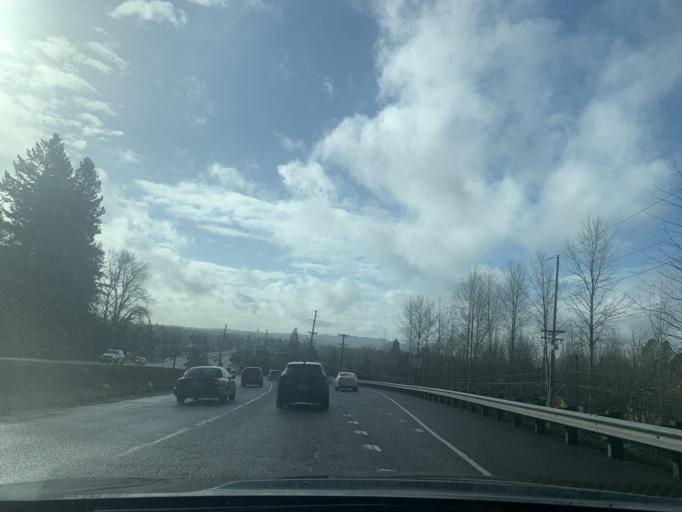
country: US
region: Oregon
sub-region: Washington County
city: King City
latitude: 45.4129
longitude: -122.7932
